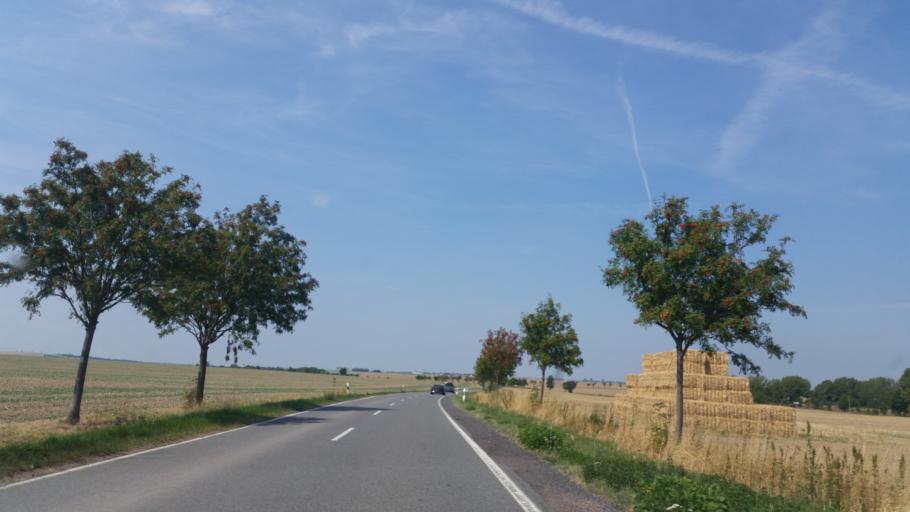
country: DE
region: Saxony
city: Wilsdruff
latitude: 51.0633
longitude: 13.5566
